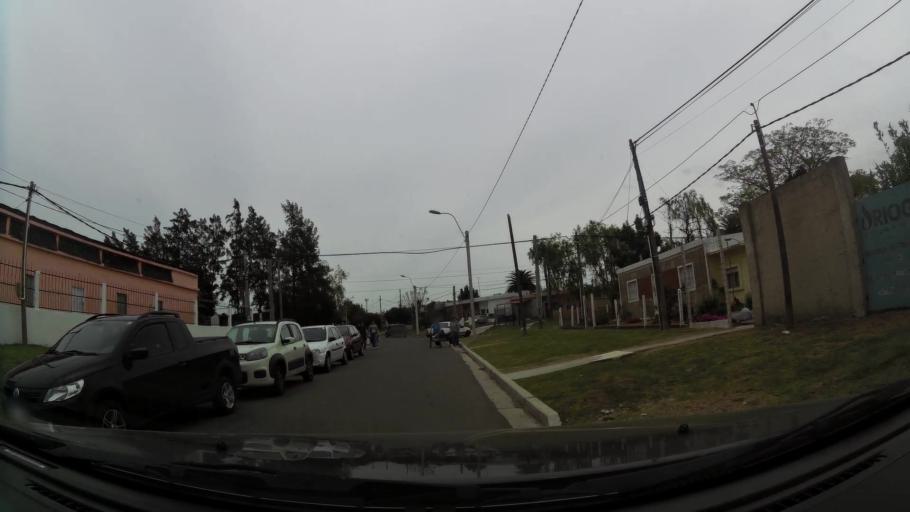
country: UY
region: Canelones
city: Las Piedras
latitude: -34.7288
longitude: -56.2095
